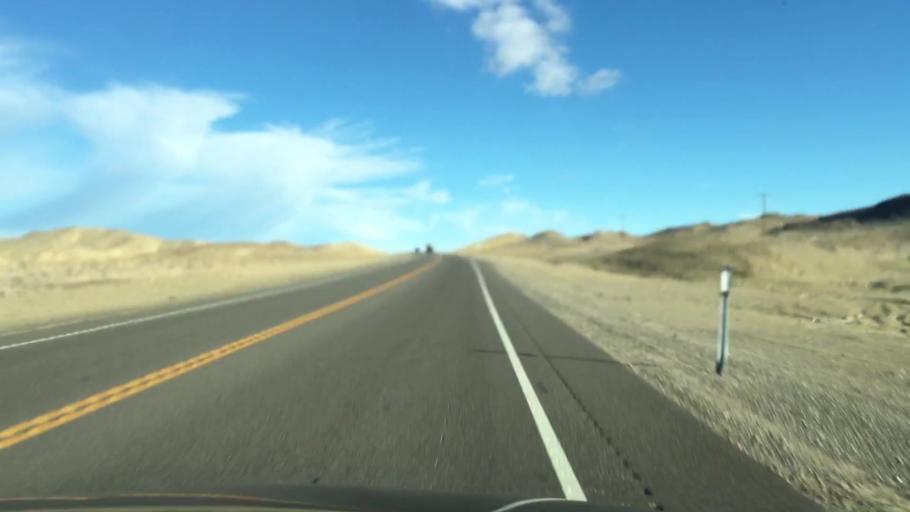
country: US
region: Nevada
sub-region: Nye County
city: Tonopah
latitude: 38.0197
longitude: -117.8532
